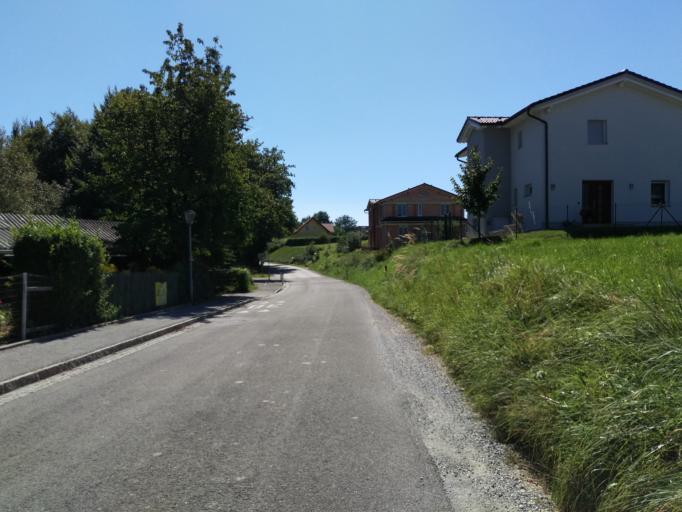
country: AT
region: Styria
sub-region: Politischer Bezirk Graz-Umgebung
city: Eggersdorf bei Graz
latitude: 47.0881
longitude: 15.5606
